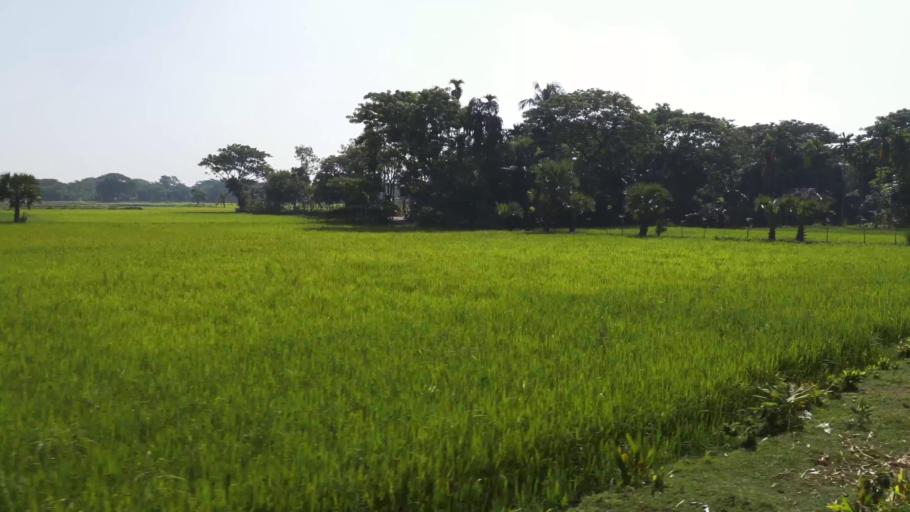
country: BD
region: Dhaka
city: Gafargaon
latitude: 24.5022
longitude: 90.5195
